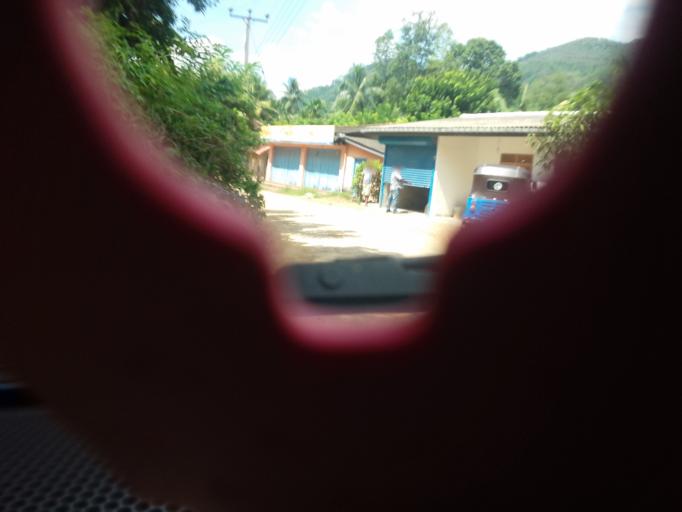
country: LK
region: Central
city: Gampola
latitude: 7.0146
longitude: 80.3546
